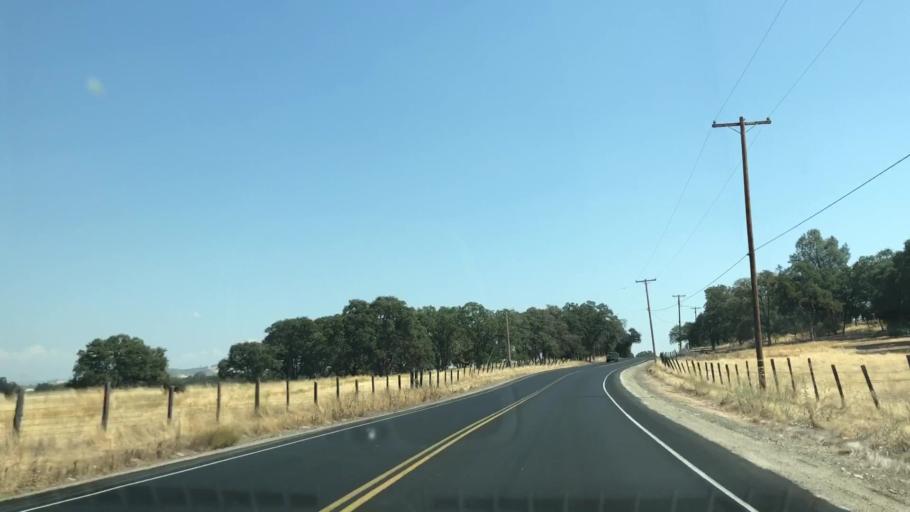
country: US
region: California
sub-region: Tuolumne County
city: Jamestown
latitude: 37.8775
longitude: -120.4454
